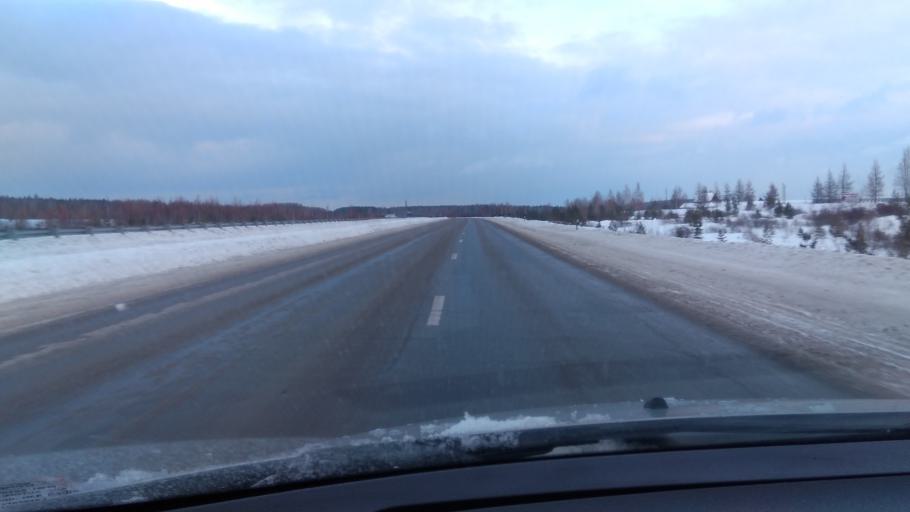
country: RU
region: Sverdlovsk
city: Nev'yansk
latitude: 57.5189
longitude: 60.1823
